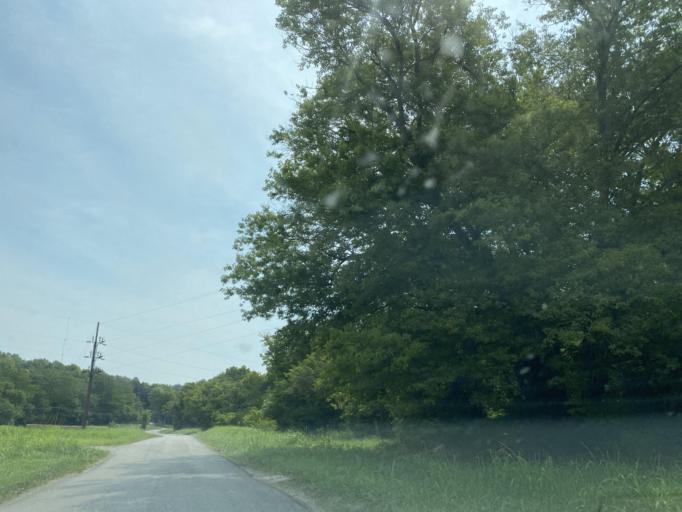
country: US
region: Kentucky
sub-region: Pendleton County
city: Falmouth
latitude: 38.7975
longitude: -84.3097
